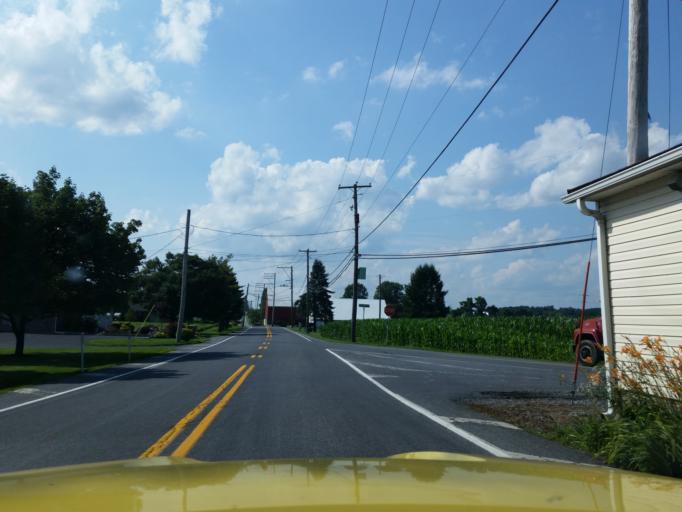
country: US
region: Pennsylvania
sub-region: Lancaster County
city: Manheim
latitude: 40.1749
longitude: -76.4567
